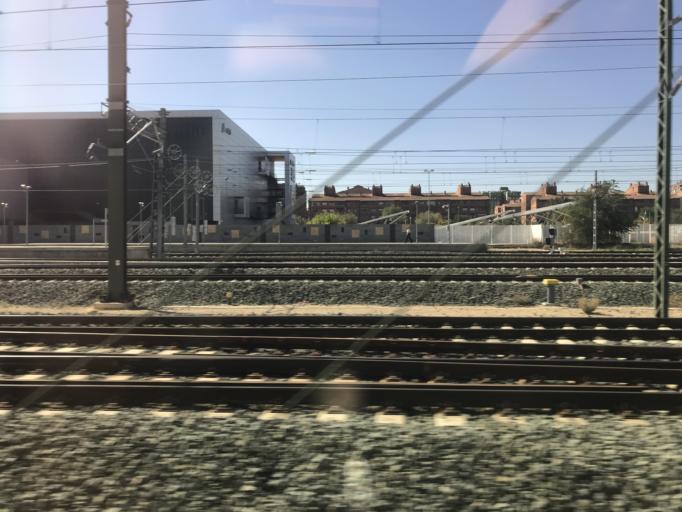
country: ES
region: Castille-La Mancha
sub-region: Provincia de Albacete
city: Albacete
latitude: 39.0011
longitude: -1.8481
